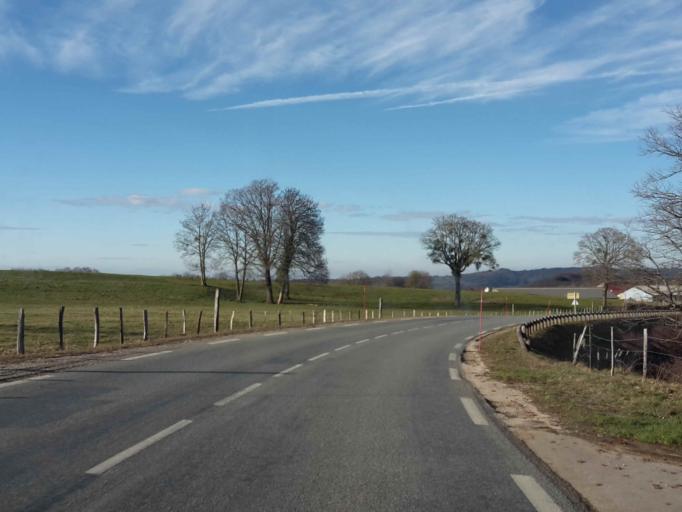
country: FR
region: Franche-Comte
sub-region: Departement du Doubs
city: Vercel-Villedieu-le-Camp
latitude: 47.2075
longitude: 6.3910
